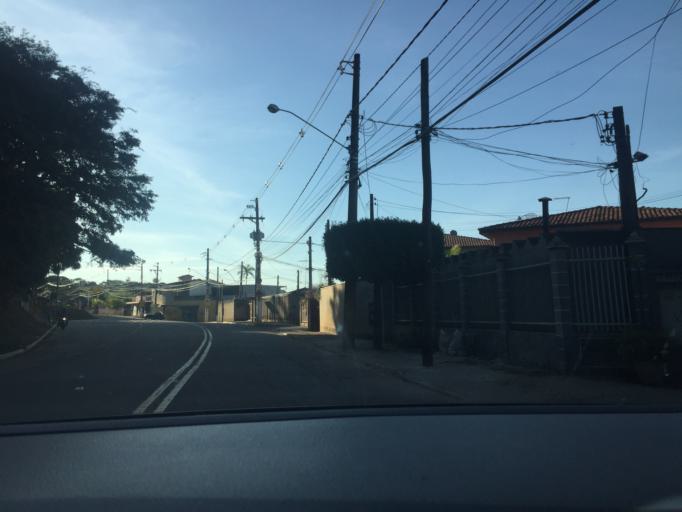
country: BR
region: Sao Paulo
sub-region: Louveira
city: Louveira
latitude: -23.1108
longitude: -46.9174
